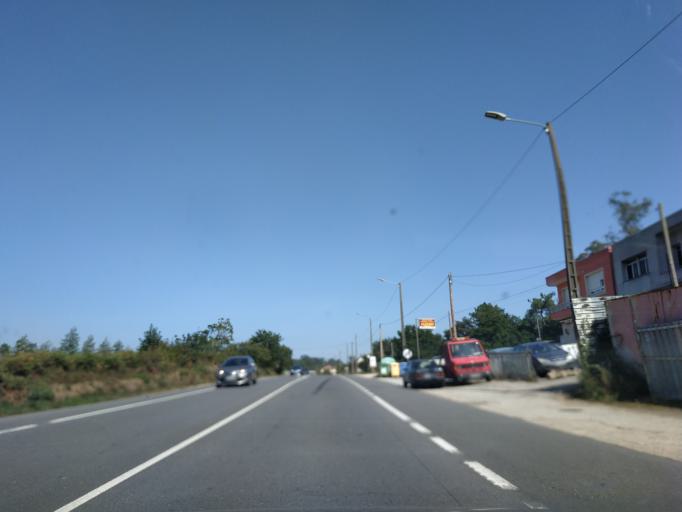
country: ES
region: Galicia
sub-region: Provincia da Coruna
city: Carballo
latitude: 43.2363
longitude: -8.6457
